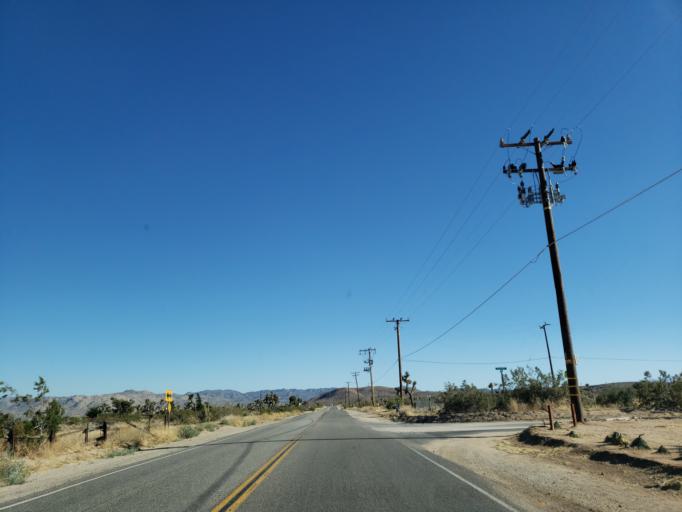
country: US
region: California
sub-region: San Bernardino County
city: Yucca Valley
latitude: 34.1828
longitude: -116.3871
